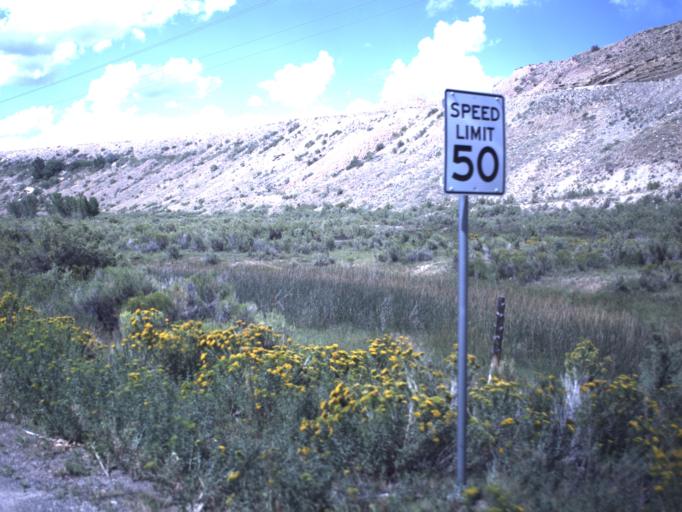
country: US
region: Utah
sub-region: Duchesne County
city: Duchesne
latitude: 40.1651
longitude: -110.4142
